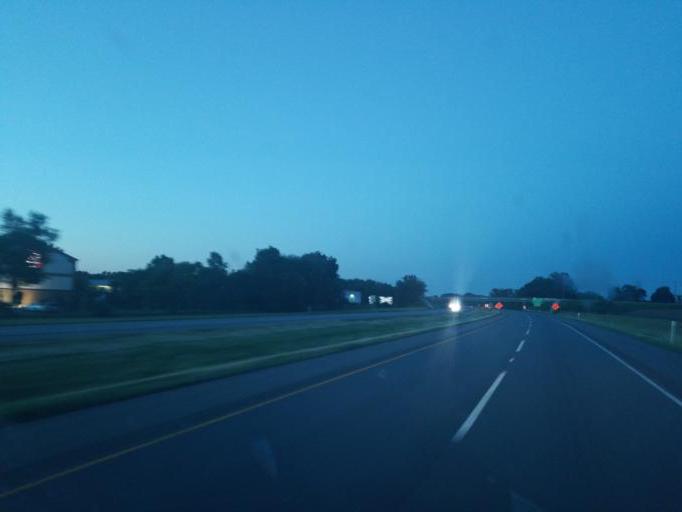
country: US
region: Indiana
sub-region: Saint Joseph County
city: Mishawaka
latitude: 41.7179
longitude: -86.1667
